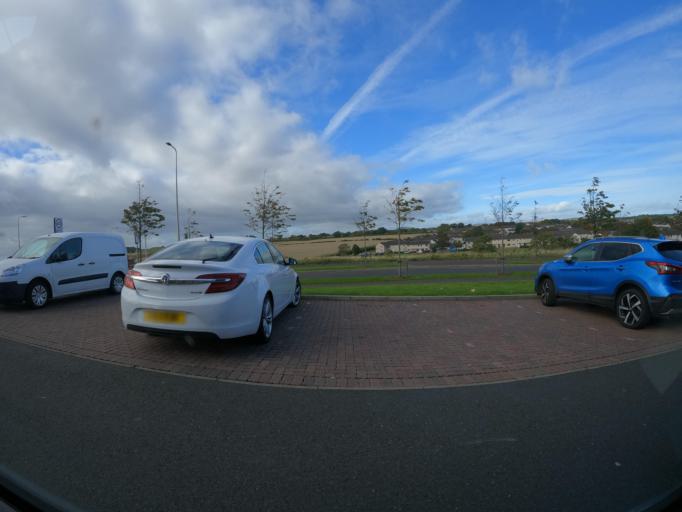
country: GB
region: Scotland
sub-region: Fife
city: Rosyth
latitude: 56.0375
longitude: -3.4381
